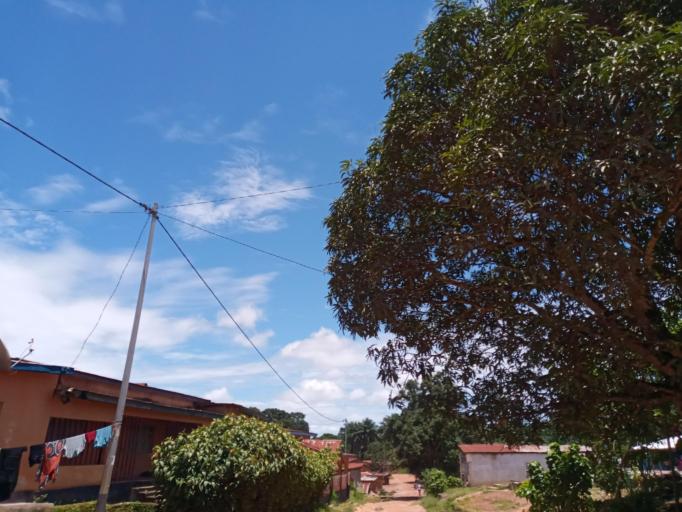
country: SL
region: Eastern Province
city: Koidu
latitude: 8.6489
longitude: -10.9630
